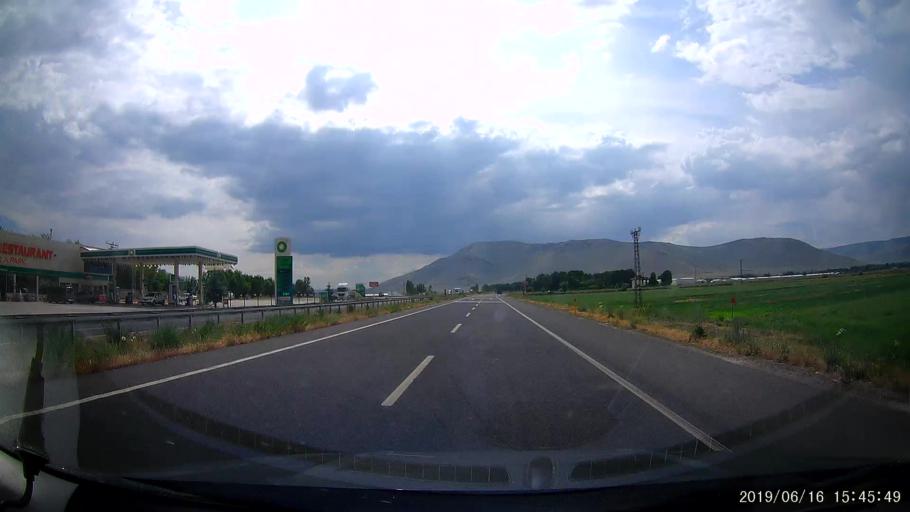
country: TR
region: Erzurum
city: Pasinler
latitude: 39.9893
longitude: 41.7577
